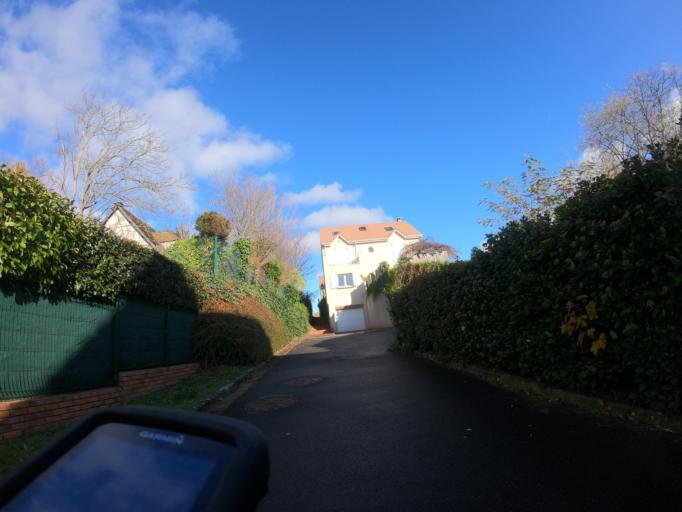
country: FR
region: Ile-de-France
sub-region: Departement de l'Essonne
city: Verrieres-le-Buisson
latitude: 48.7542
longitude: 2.2808
